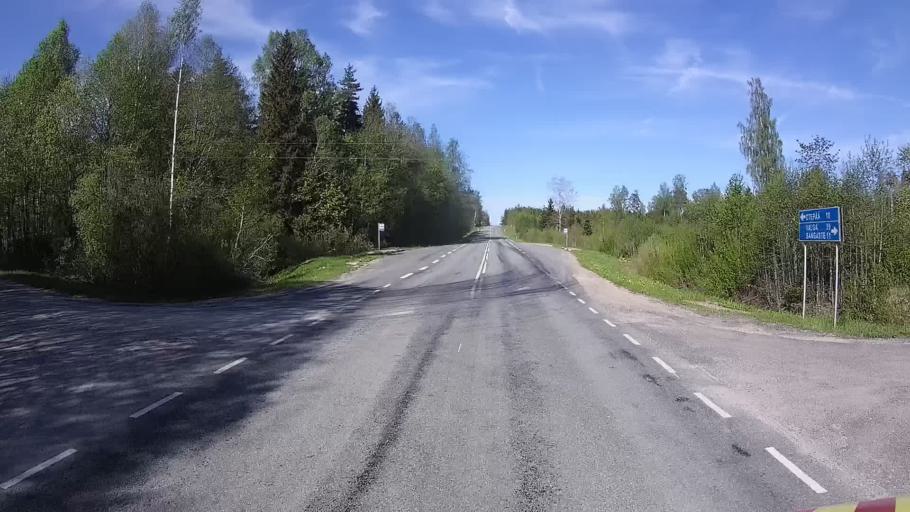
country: EE
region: Vorumaa
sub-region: Antsla vald
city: Vana-Antsla
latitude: 57.9811
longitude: 26.4692
